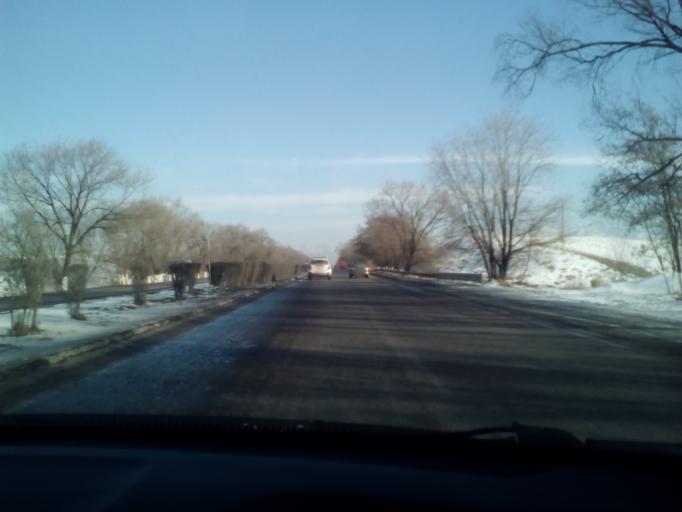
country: KZ
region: Almaty Oblysy
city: Burunday
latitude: 43.2221
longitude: 76.4324
